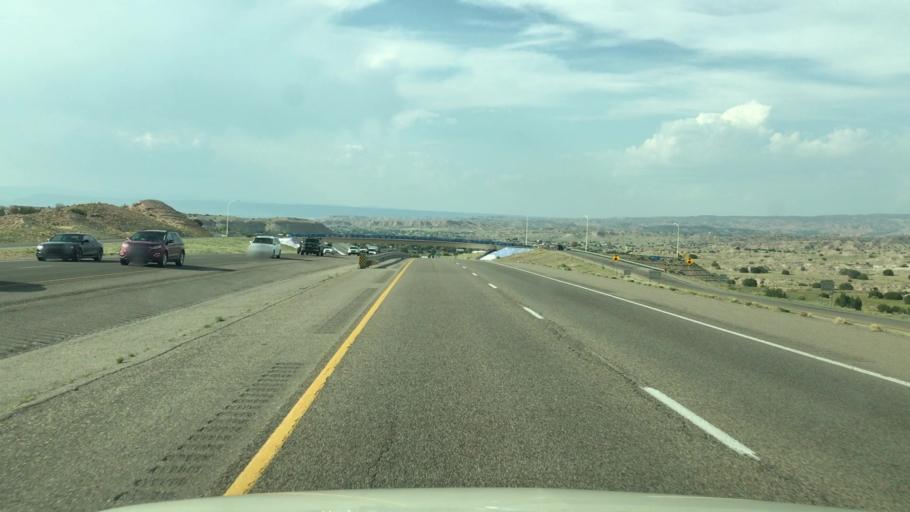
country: US
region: New Mexico
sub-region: Santa Fe County
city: Pojoaque
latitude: 35.9259
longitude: -106.0173
